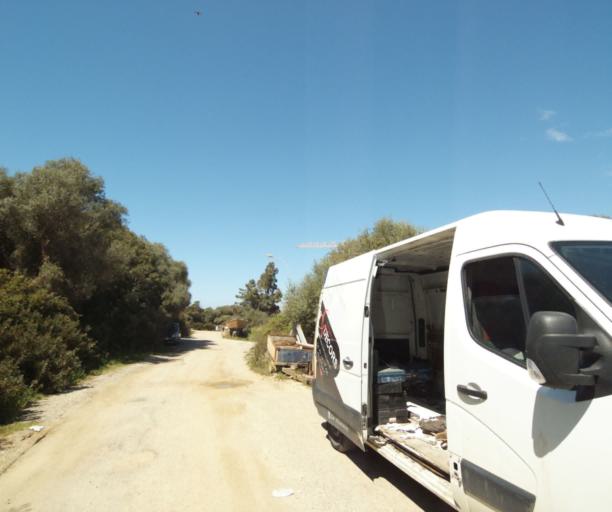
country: FR
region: Corsica
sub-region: Departement de la Corse-du-Sud
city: Propriano
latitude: 41.6533
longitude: 8.9002
